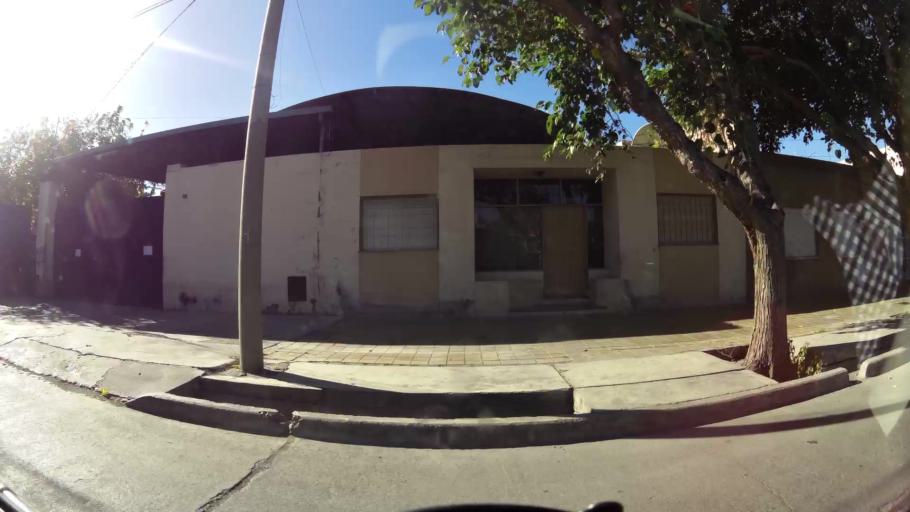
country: AR
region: San Juan
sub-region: Departamento de Santa Lucia
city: Santa Lucia
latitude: -31.5345
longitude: -68.5123
